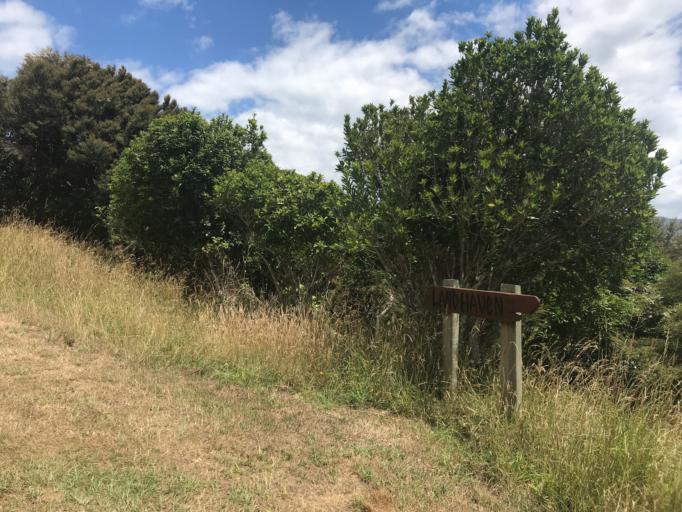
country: NZ
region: Marlborough
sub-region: Marlborough District
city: Picton
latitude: -41.2132
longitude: 173.9958
